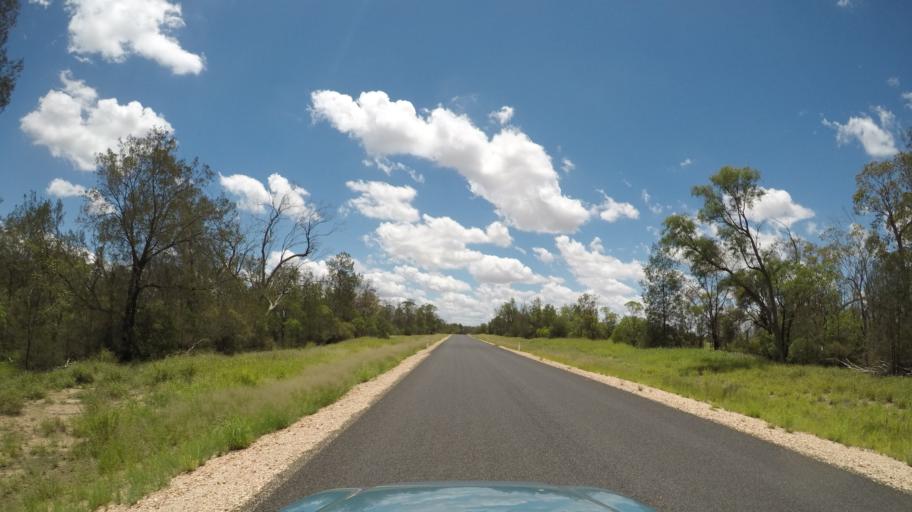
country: AU
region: Queensland
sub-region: Goondiwindi
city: Goondiwindi
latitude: -28.1533
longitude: 150.1242
